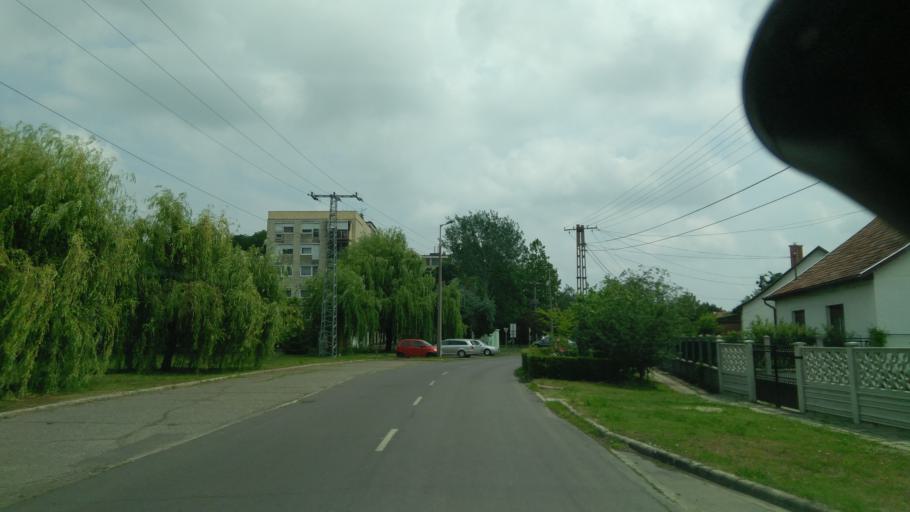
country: HU
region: Bekes
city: Gyula
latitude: 46.6556
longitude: 21.2596
